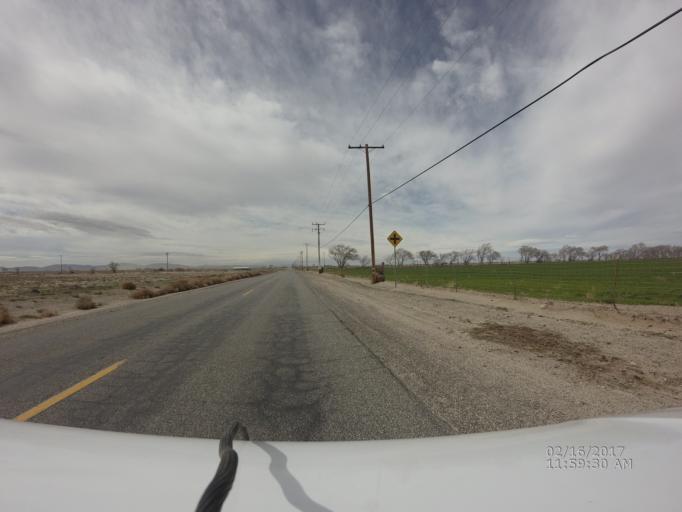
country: US
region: California
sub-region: Los Angeles County
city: Lake Los Angeles
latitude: 34.6901
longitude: -117.9323
